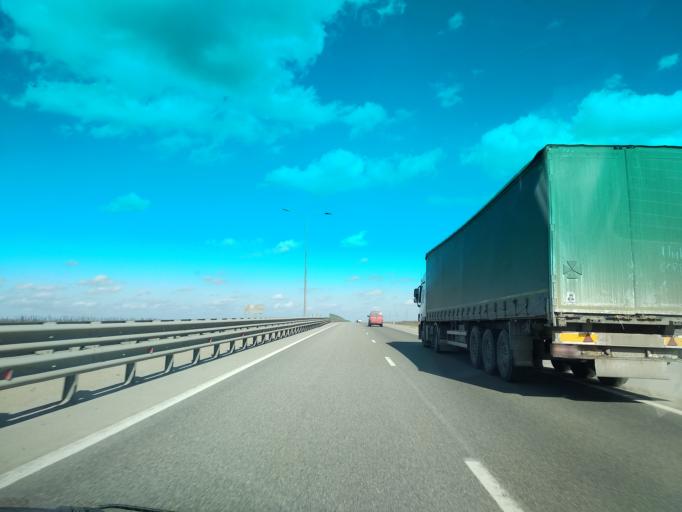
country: RU
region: Krasnodarskiy
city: Dinskaya
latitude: 45.2583
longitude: 39.2035
